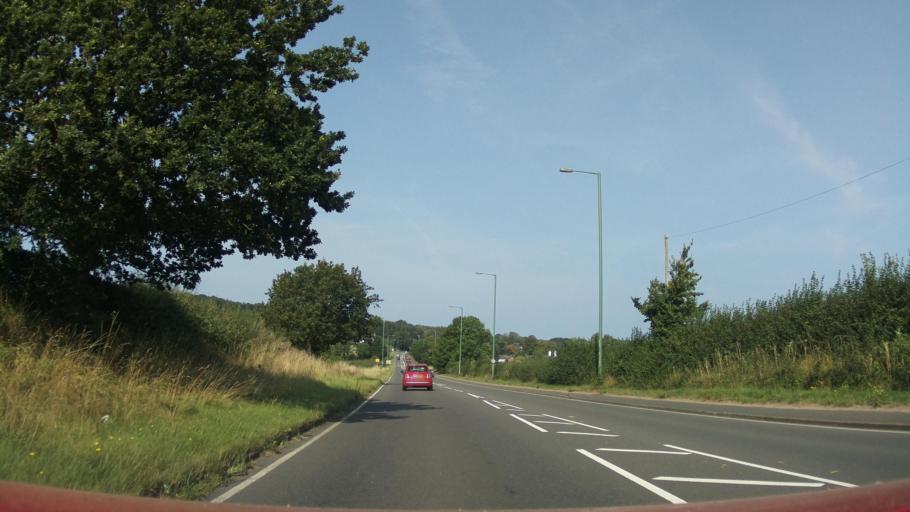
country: GB
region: England
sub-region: Walsall
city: Aldridge
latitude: 52.6247
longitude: -1.8976
